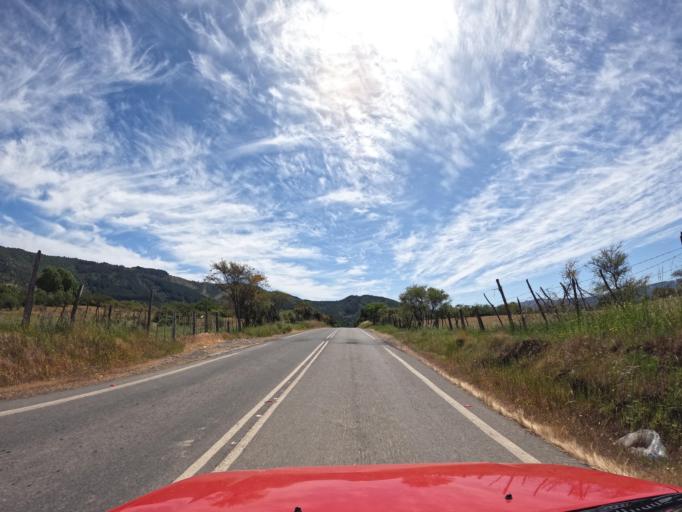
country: CL
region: Maule
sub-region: Provincia de Talca
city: Talca
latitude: -35.0016
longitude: -71.8002
